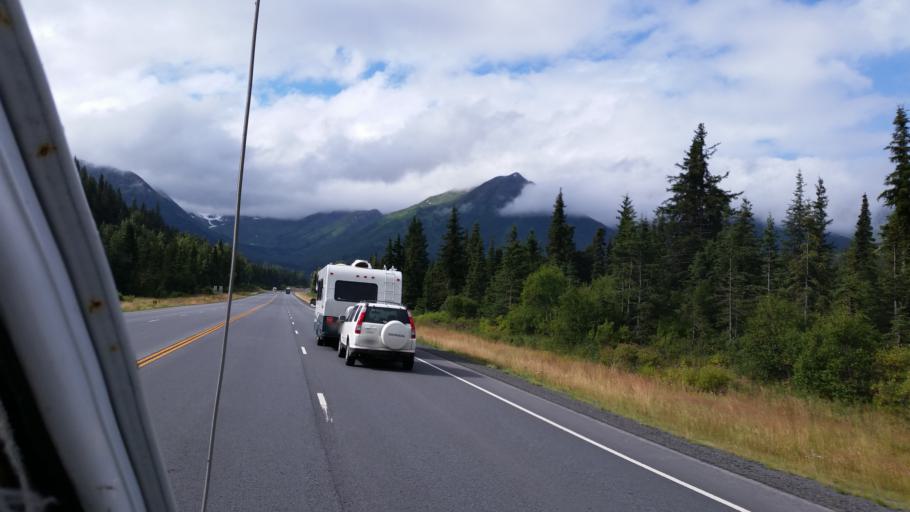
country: US
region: Alaska
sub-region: Anchorage Municipality
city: Girdwood
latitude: 60.7399
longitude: -149.2613
